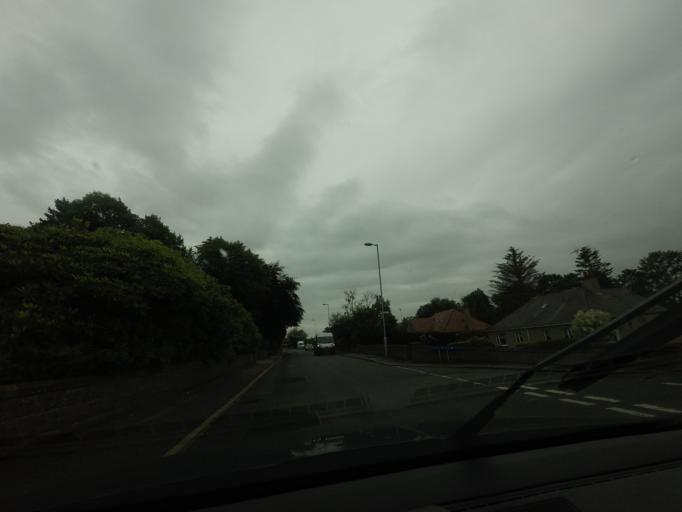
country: GB
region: Scotland
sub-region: Aberdeenshire
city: Turriff
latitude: 57.5403
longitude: -2.4709
